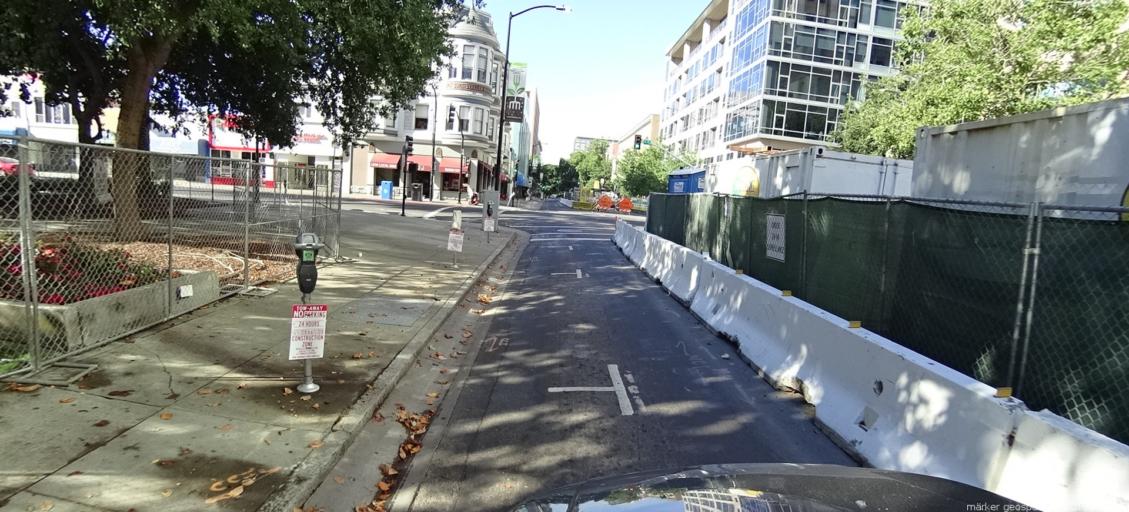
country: US
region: California
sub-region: Sacramento County
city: Sacramento
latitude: 38.5810
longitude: -121.4946
